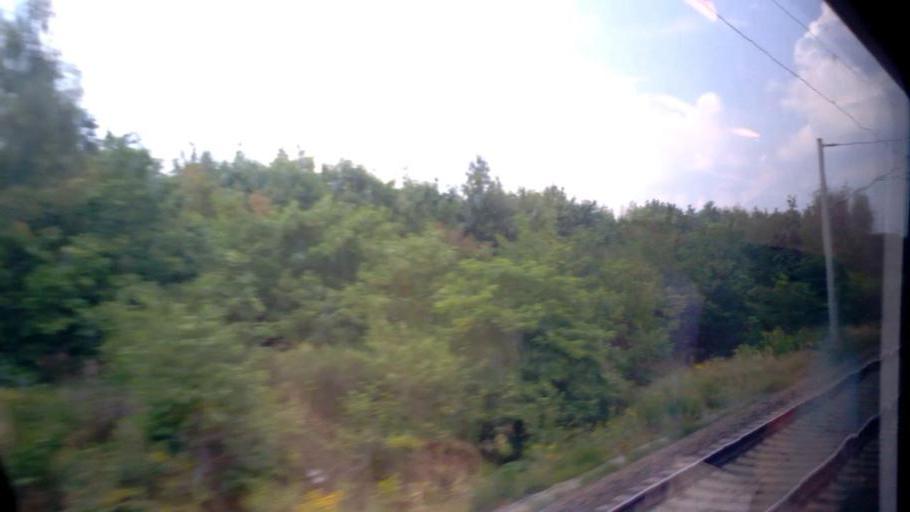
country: DE
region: Brandenburg
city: Grossbeeren
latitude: 52.3698
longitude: 13.2925
